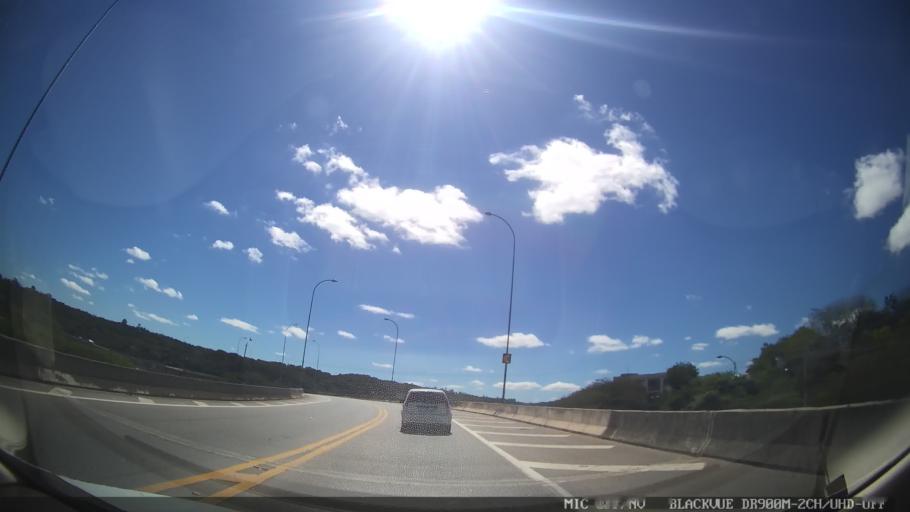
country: BR
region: Sao Paulo
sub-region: Campo Limpo Paulista
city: Campo Limpo Paulista
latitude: -23.2029
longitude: -46.7939
